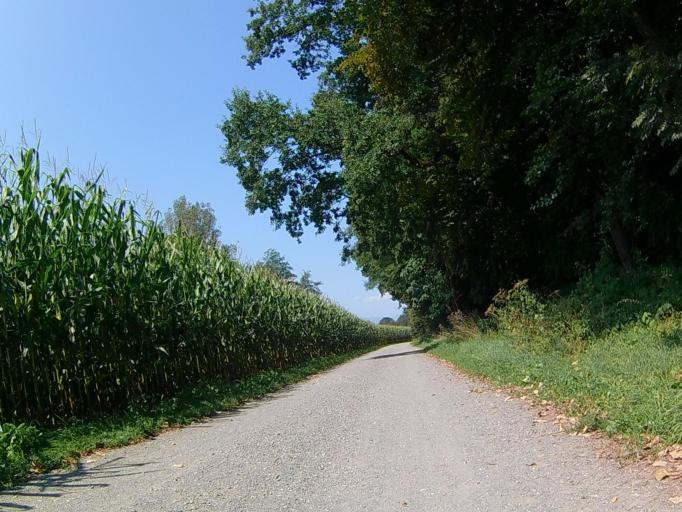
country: AT
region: Styria
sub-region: Politischer Bezirk Leibnitz
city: Oberhaag
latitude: 46.6881
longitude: 15.3479
